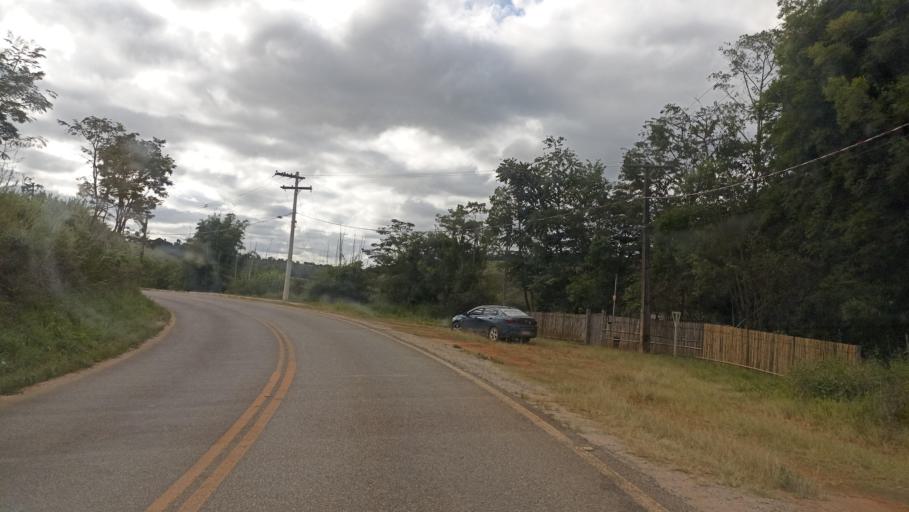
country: BR
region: Minas Gerais
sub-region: Tiradentes
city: Tiradentes
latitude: -21.0747
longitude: -44.0756
